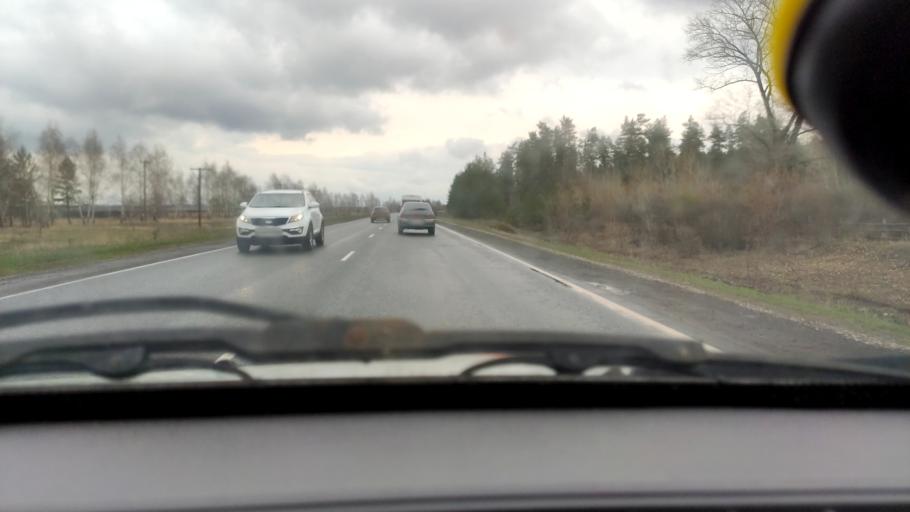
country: RU
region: Samara
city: Povolzhskiy
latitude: 53.5982
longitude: 49.5907
